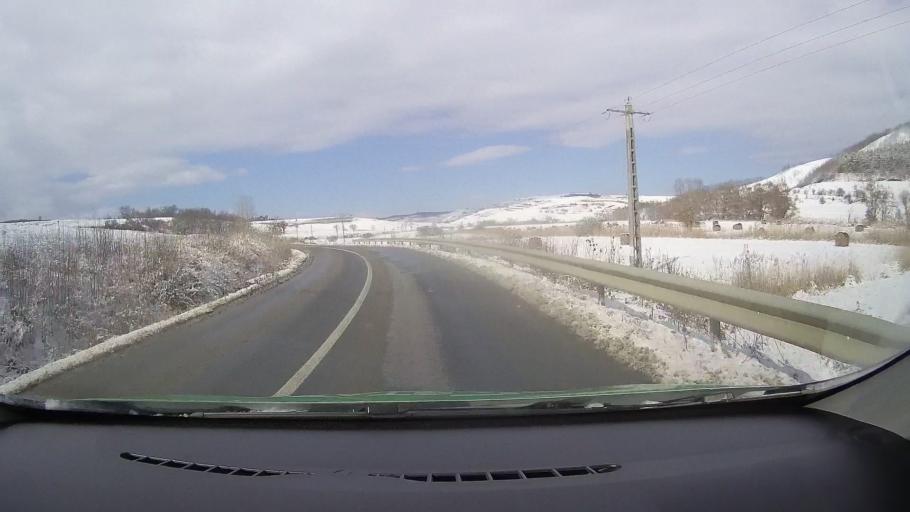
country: RO
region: Sibiu
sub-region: Comuna Altina
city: Altina
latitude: 45.9690
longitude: 24.4699
